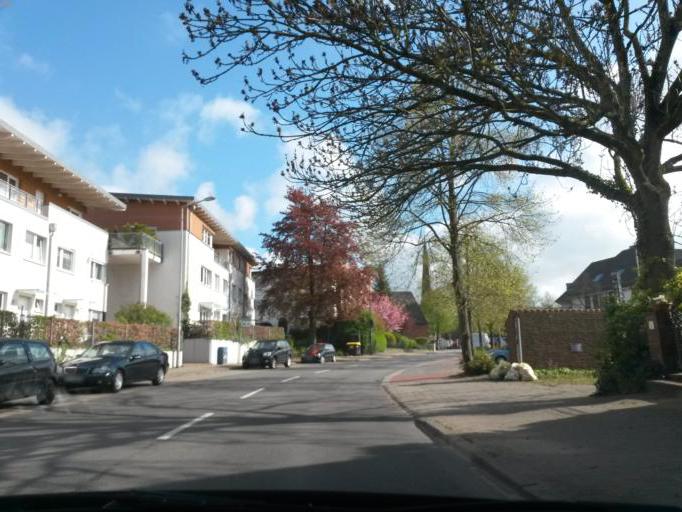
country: DE
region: Schleswig-Holstein
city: Wedel
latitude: 53.5829
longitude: 9.6964
